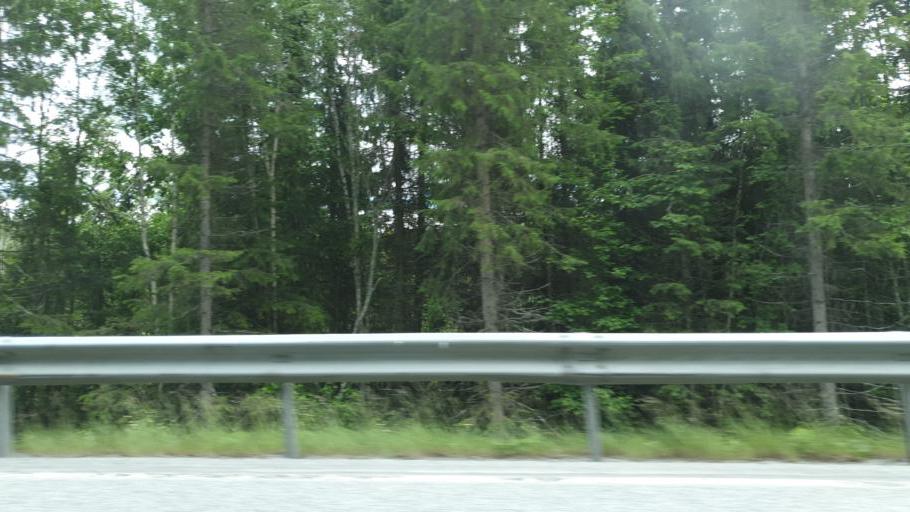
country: NO
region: Sor-Trondelag
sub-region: Rennebu
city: Berkak
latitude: 62.8728
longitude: 10.0852
